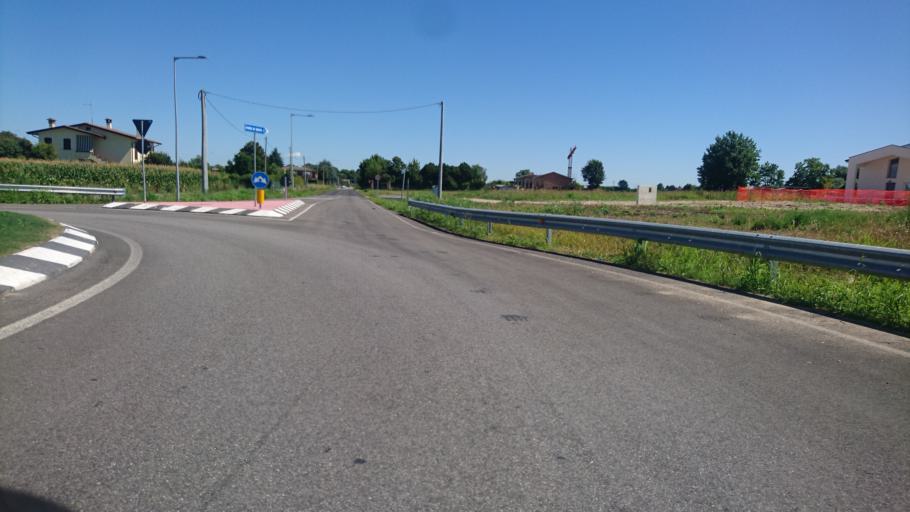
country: IT
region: Veneto
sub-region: Provincia di Padova
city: Campagnola
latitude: 45.2774
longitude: 12.0190
